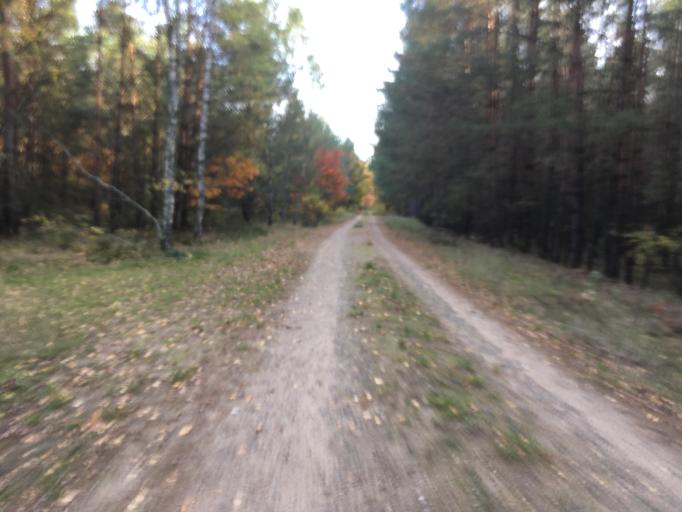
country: DE
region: Brandenburg
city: Birkenwerder
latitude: 52.6953
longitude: 13.3432
